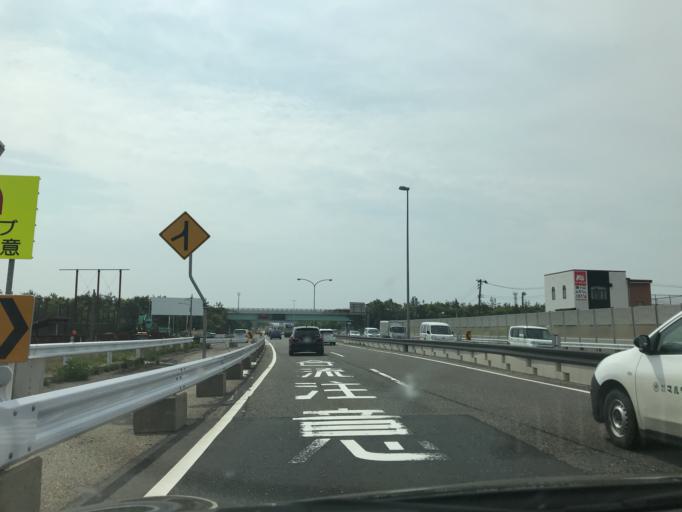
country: JP
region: Niigata
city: Kameda-honcho
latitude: 37.8828
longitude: 139.0804
